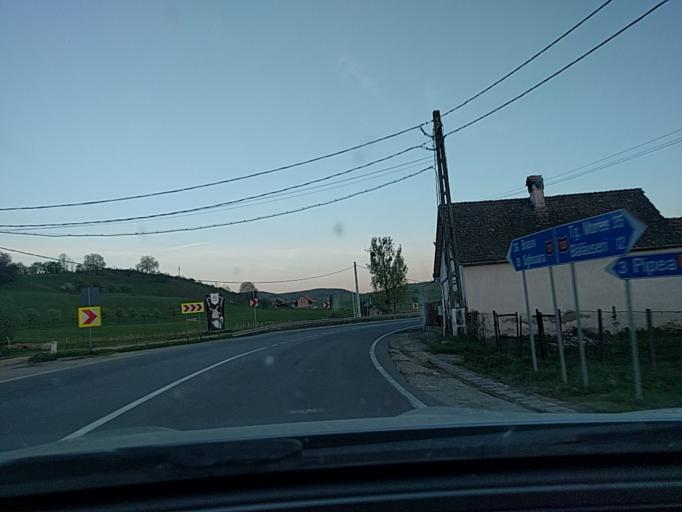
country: RO
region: Mures
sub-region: Comuna Nades
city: Nades
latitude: 46.3188
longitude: 24.7224
